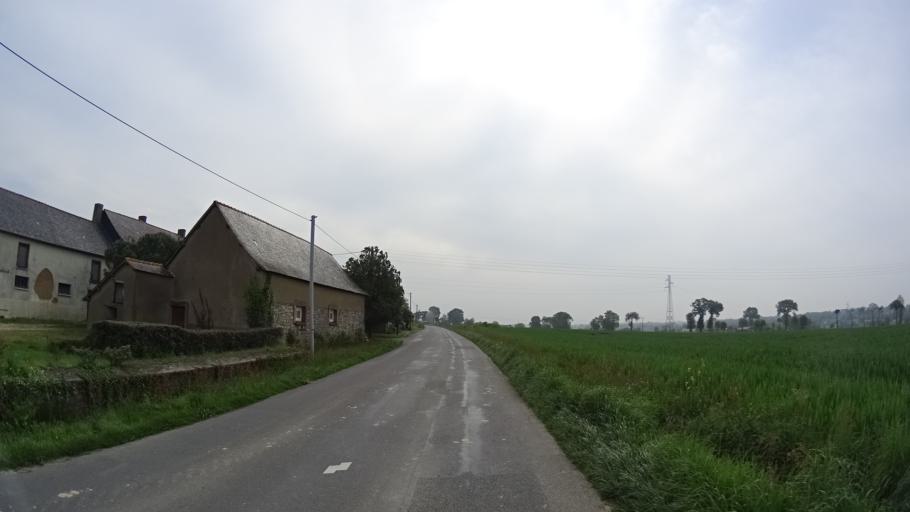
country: FR
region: Brittany
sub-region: Departement d'Ille-et-Vilaine
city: Montreuil-le-Gast
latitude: 48.2479
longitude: -1.7396
